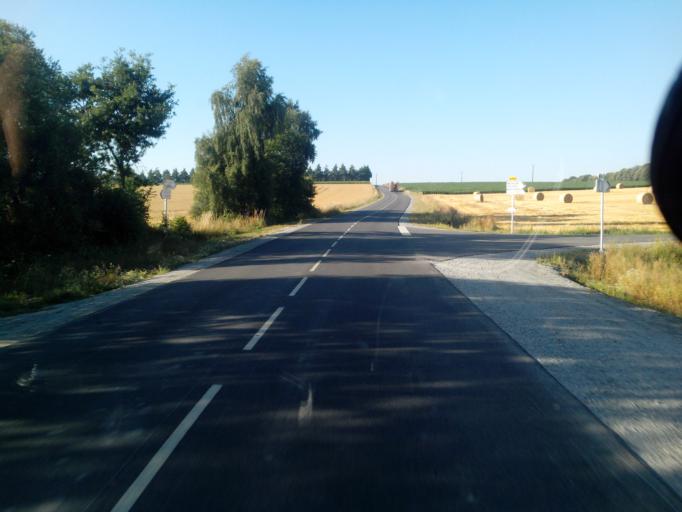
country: FR
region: Brittany
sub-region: Departement du Morbihan
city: Meneac
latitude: 48.1169
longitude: -2.4585
